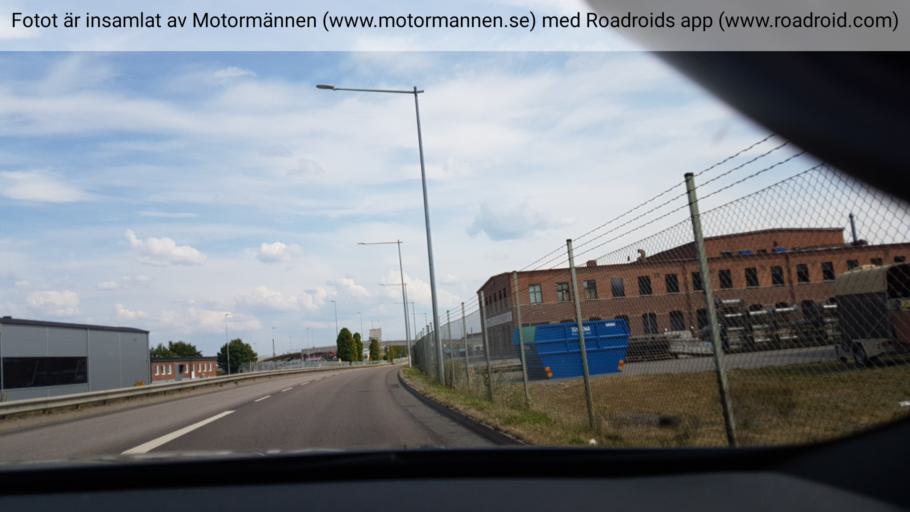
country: SE
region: Vaestra Goetaland
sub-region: Lidkopings Kommun
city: Lidkoping
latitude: 58.5038
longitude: 13.1653
